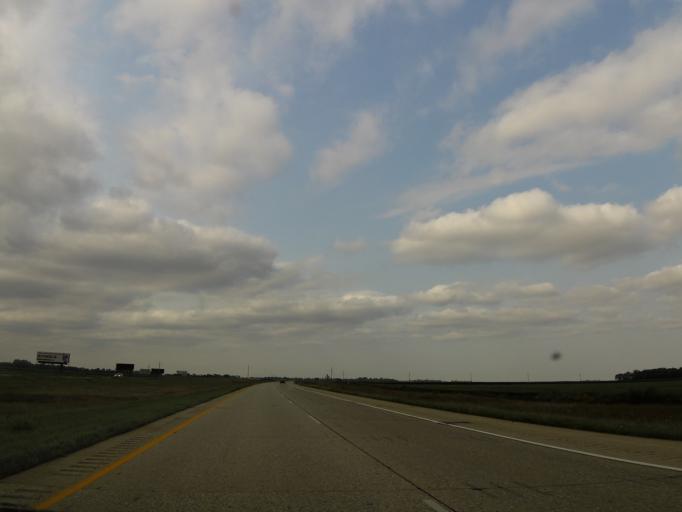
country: US
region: North Dakota
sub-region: Richland County
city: Wahpeton
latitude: 46.2771
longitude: -96.8333
